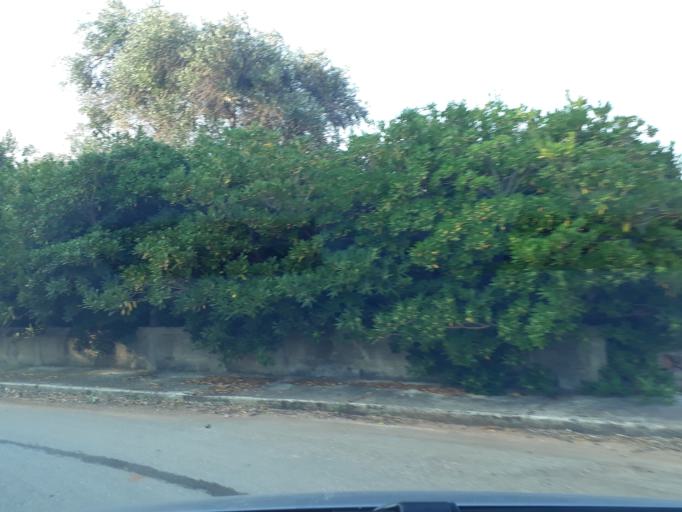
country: IT
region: Apulia
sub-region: Provincia di Brindisi
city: Carovigno
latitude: 40.7483
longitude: 17.7106
